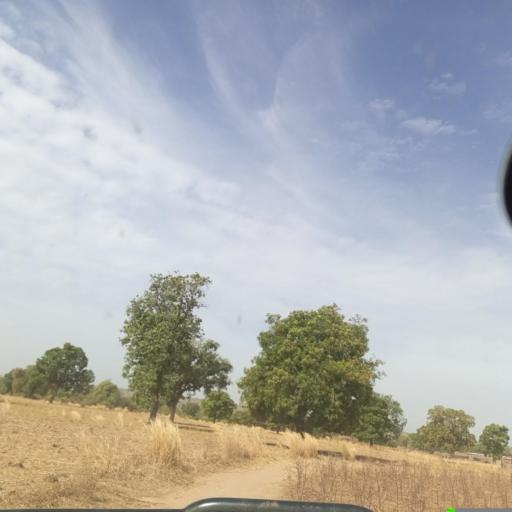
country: ML
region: Koulikoro
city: Koulikoro
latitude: 13.1256
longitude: -7.7070
